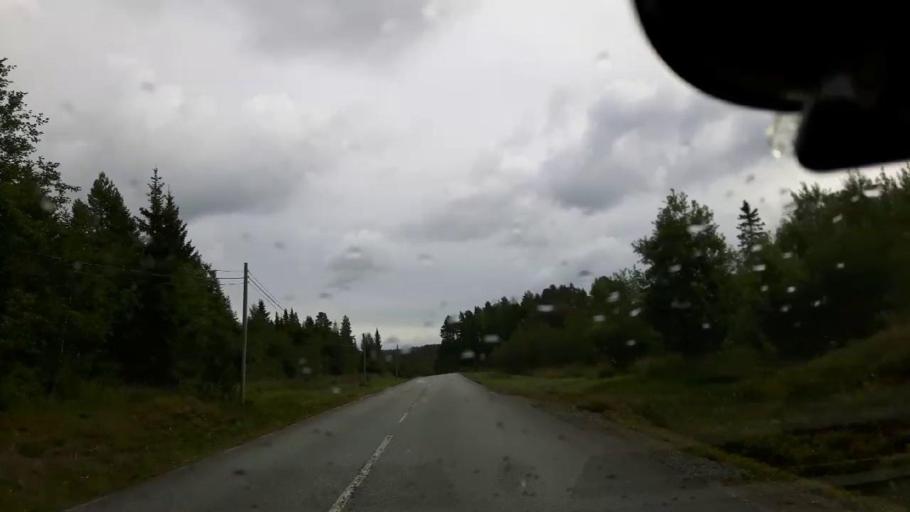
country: SE
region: Jaemtland
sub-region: Krokoms Kommun
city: Valla
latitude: 63.3983
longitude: 13.8144
